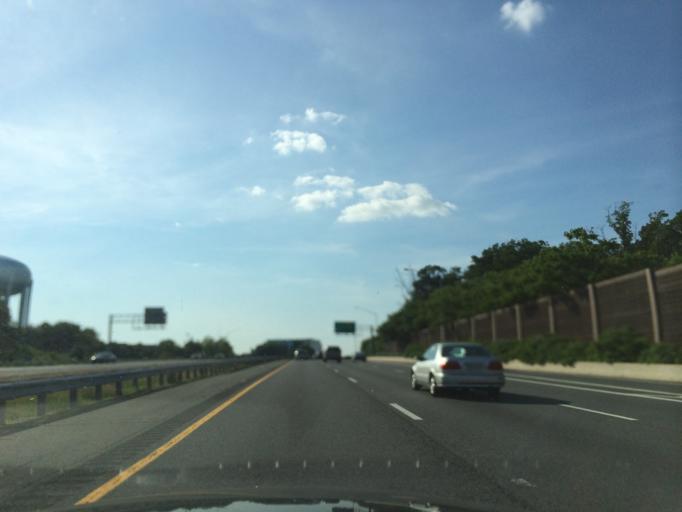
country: US
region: Maryland
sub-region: Howard County
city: Columbia
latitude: 39.2273
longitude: -76.8096
